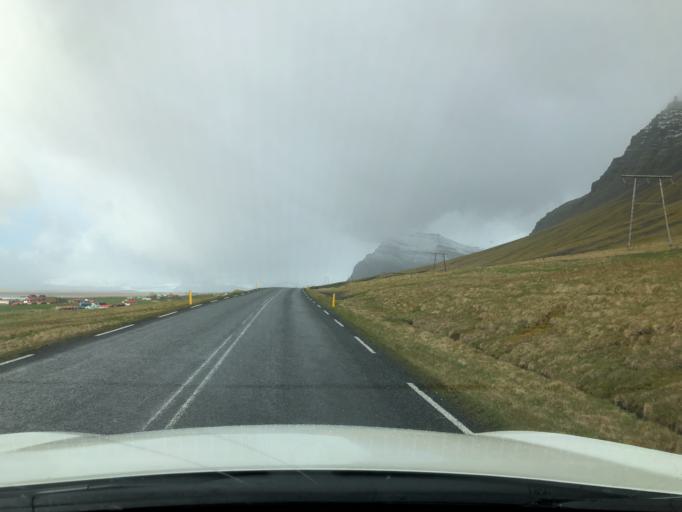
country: IS
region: East
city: Hoefn
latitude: 64.1331
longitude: -15.9985
